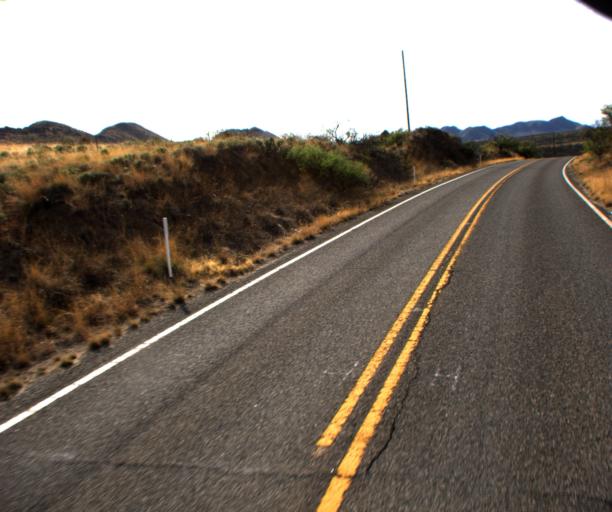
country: US
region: Arizona
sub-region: Cochise County
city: Willcox
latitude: 32.1722
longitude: -109.6005
